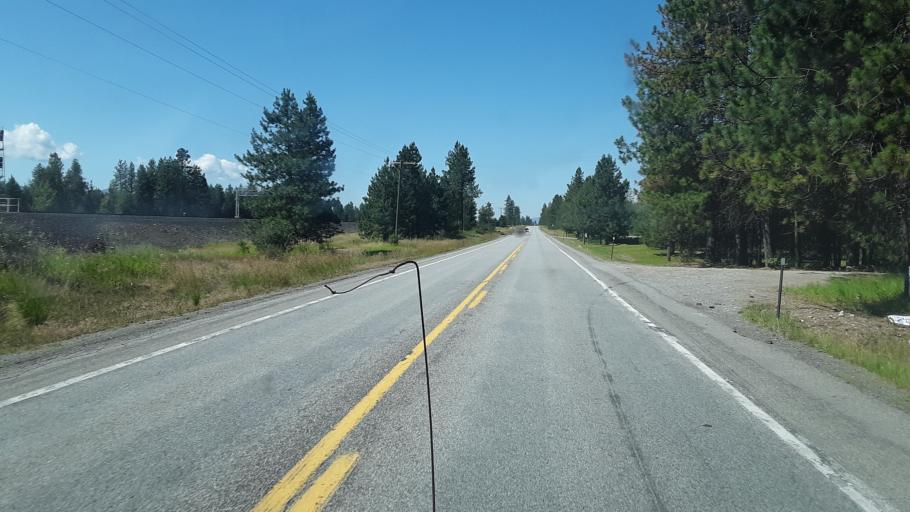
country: US
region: Idaho
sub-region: Kootenai County
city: Rathdrum
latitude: 47.7997
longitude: -116.9191
